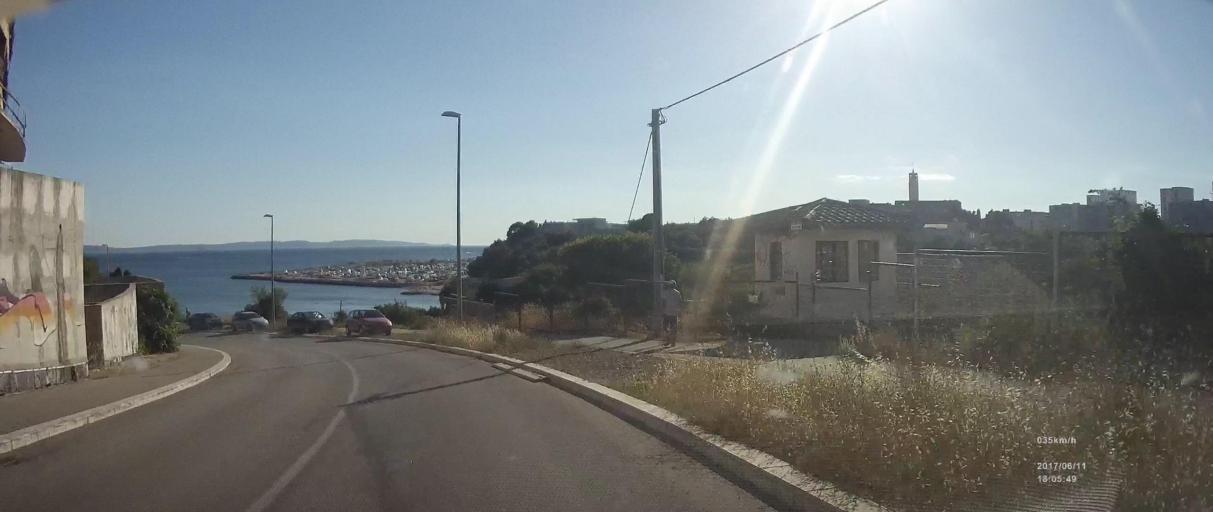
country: HR
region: Splitsko-Dalmatinska
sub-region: Grad Split
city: Split
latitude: 43.5031
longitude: 16.4682
